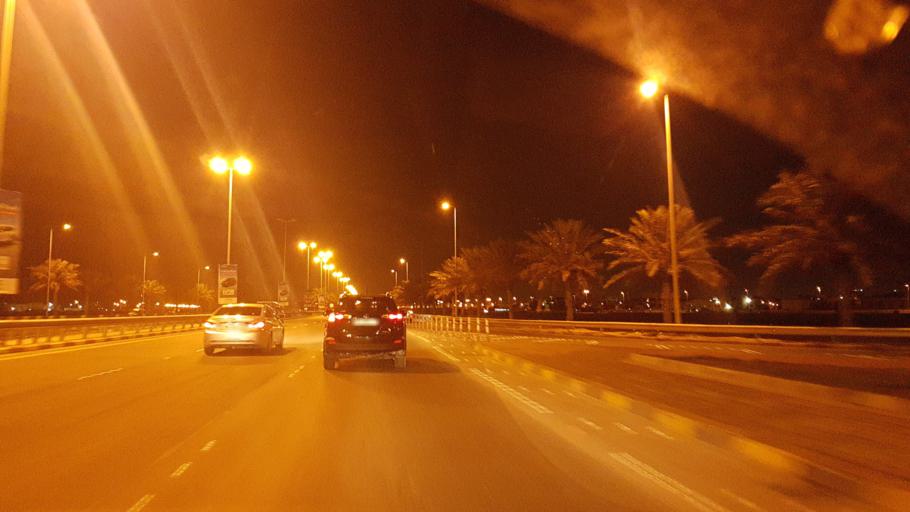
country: BH
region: Muharraq
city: Al Hadd
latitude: 26.2538
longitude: 50.6596
